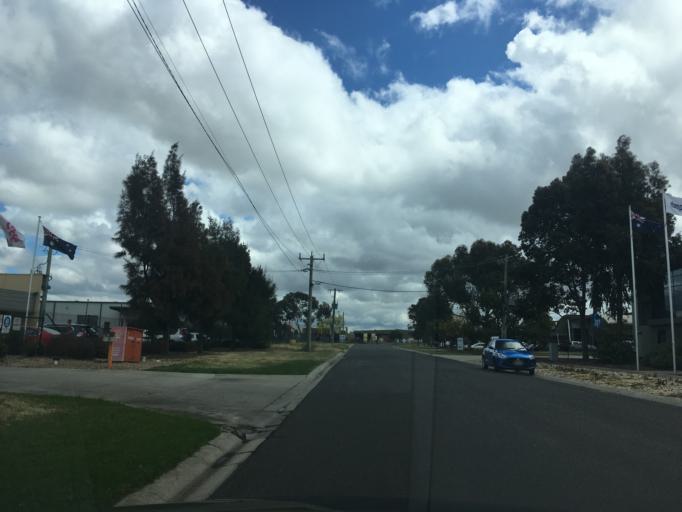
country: AU
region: Victoria
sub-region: Brimbank
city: Sunshine West
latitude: -37.8181
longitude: 144.7946
